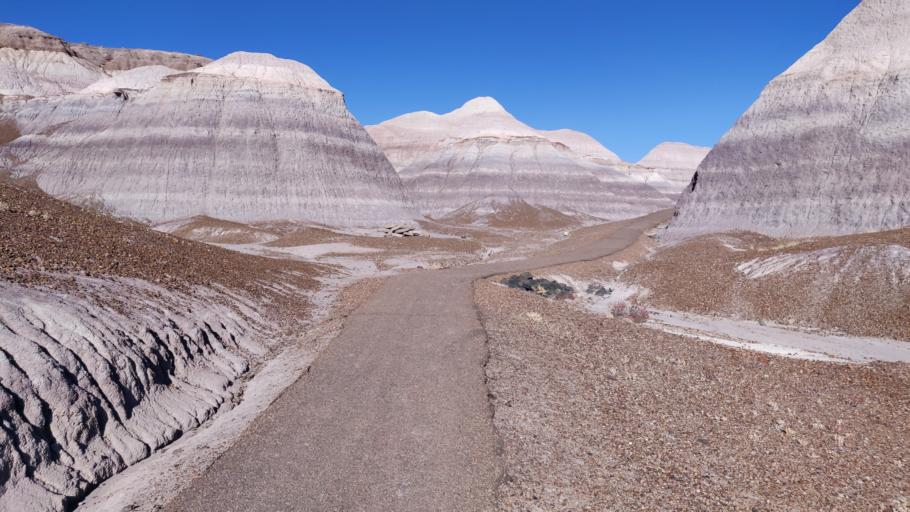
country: US
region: Arizona
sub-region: Navajo County
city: Holbrook
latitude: 34.9387
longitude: -109.7598
